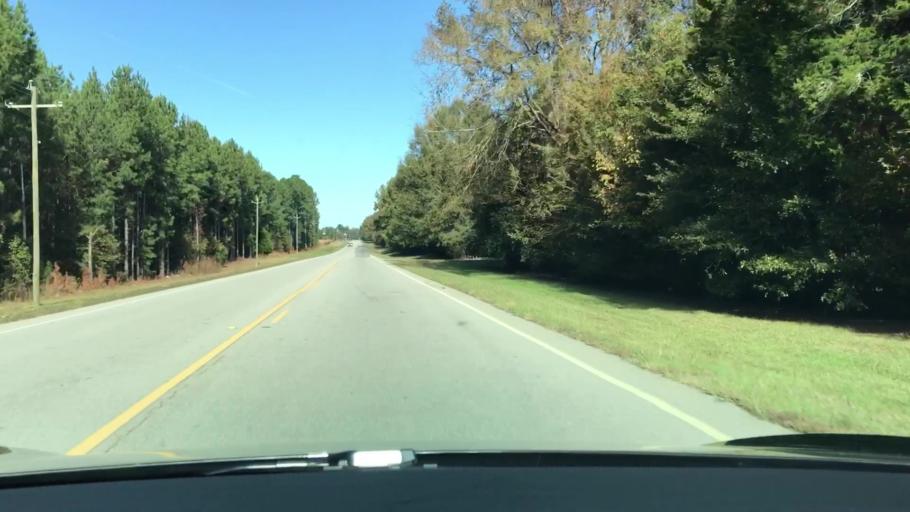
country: US
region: Georgia
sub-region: Warren County
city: Firing Range
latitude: 33.4437
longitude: -82.6930
